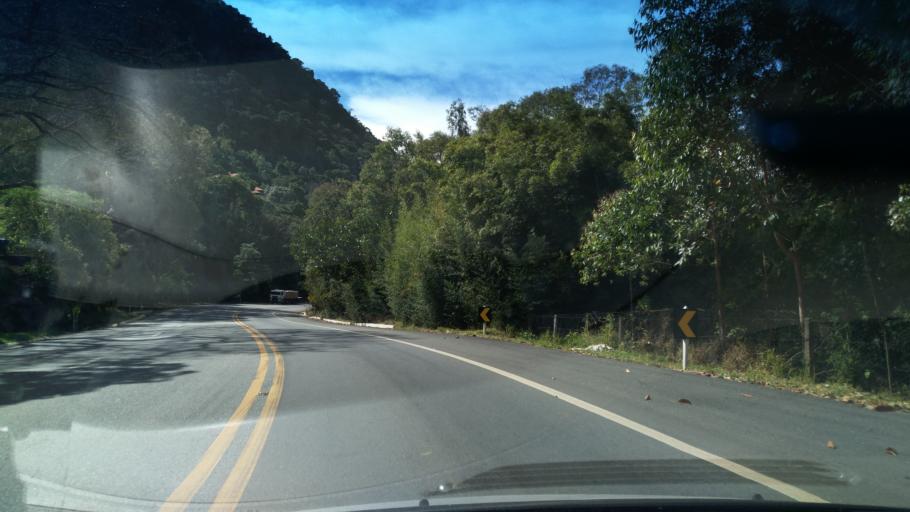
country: BR
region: Minas Gerais
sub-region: Borda Da Mata
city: Borda da Mata
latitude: -22.1314
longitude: -46.1810
